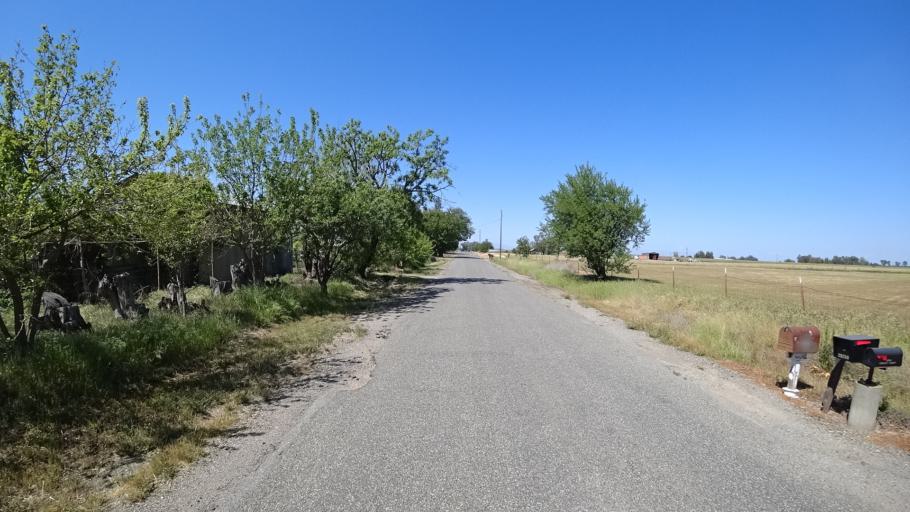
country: US
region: California
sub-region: Glenn County
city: Orland
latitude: 39.7977
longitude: -122.1518
